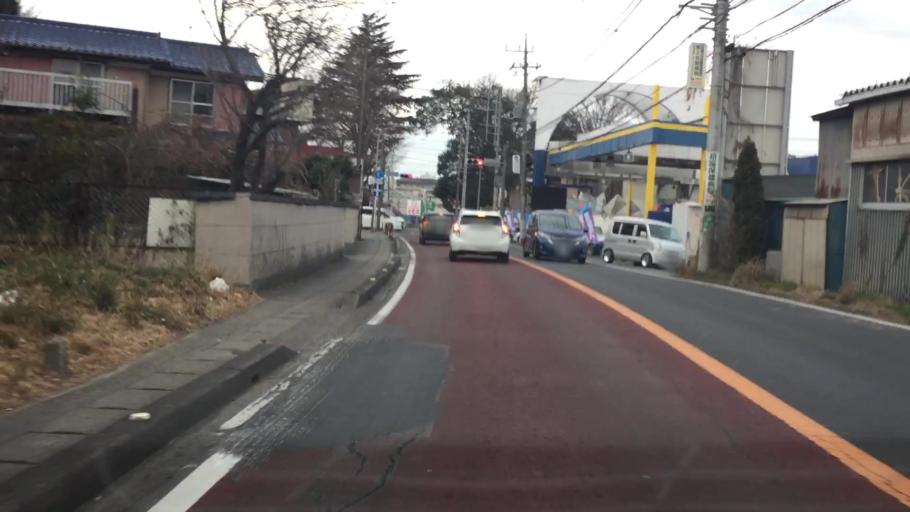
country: JP
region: Chiba
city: Shiroi
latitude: 35.7862
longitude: 140.0027
